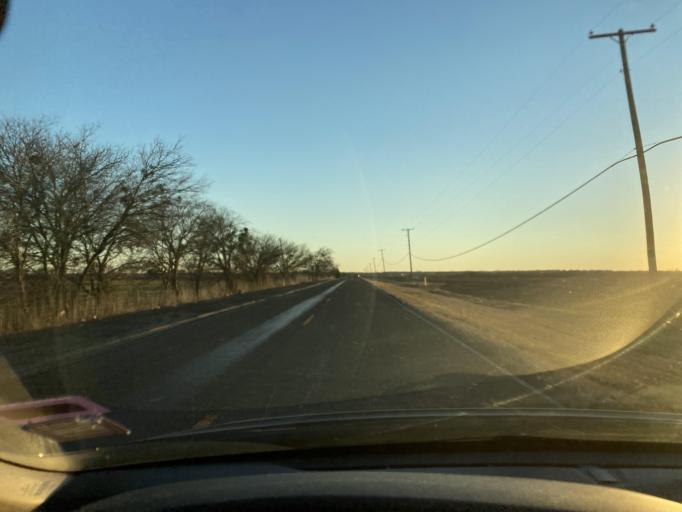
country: US
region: Texas
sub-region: Ellis County
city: Waxahachie
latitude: 32.3647
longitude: -96.8648
